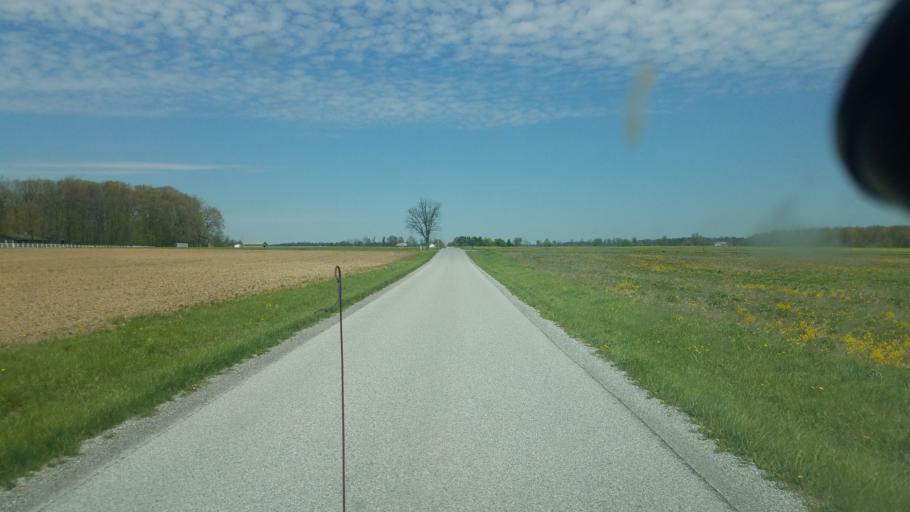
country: US
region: Ohio
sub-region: Allen County
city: Bluffton
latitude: 40.8111
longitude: -83.8991
